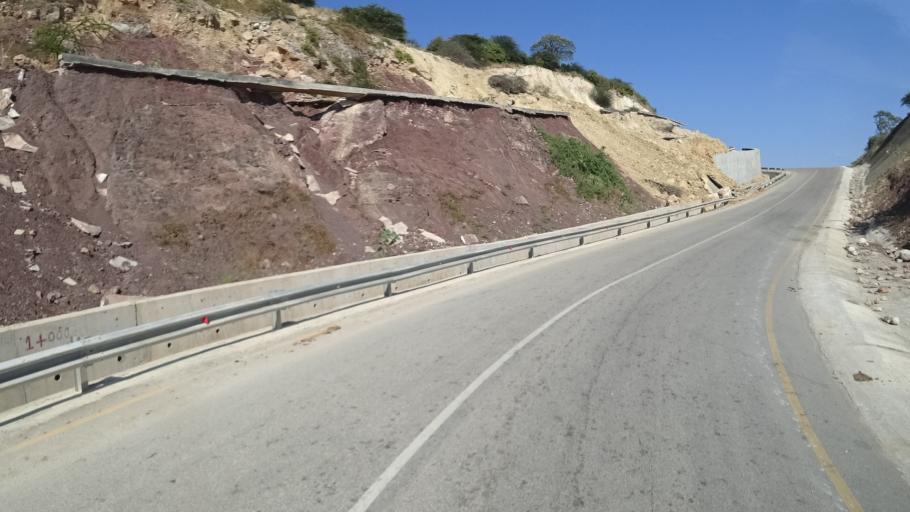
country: OM
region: Zufar
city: Salalah
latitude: 17.0543
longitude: 54.6108
